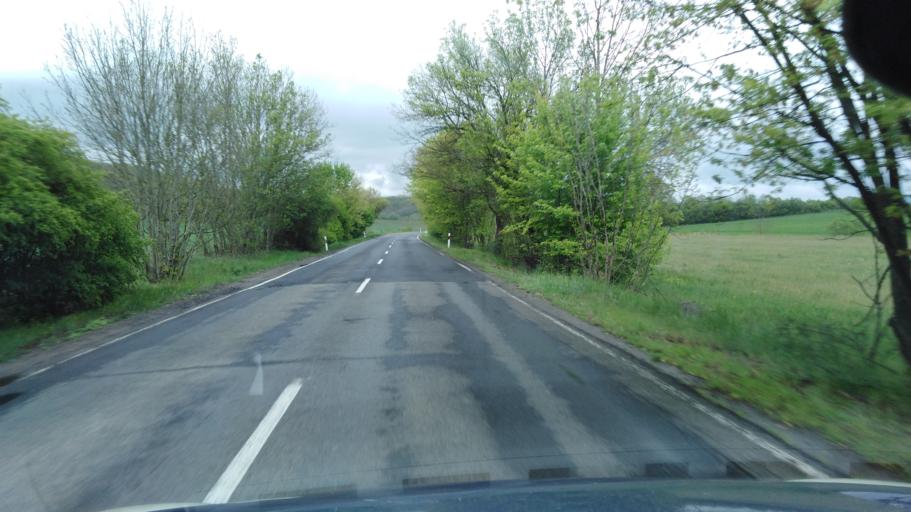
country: HU
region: Nograd
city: Szecseny
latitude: 48.1233
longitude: 19.5535
